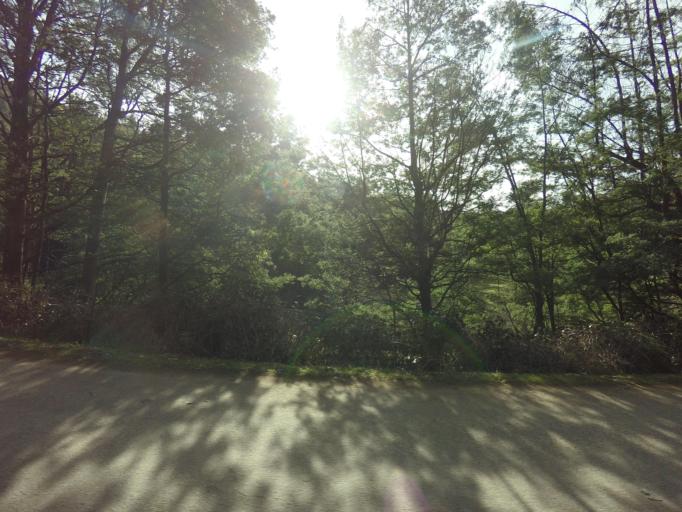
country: AU
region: Tasmania
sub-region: Huon Valley
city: Huonville
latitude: -43.0366
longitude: 147.1403
